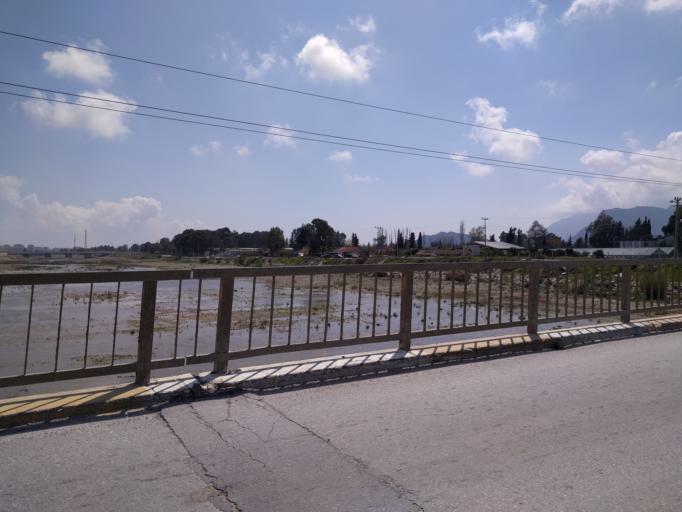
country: TR
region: Antalya
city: Cakirlar
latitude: 36.8940
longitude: 30.6045
